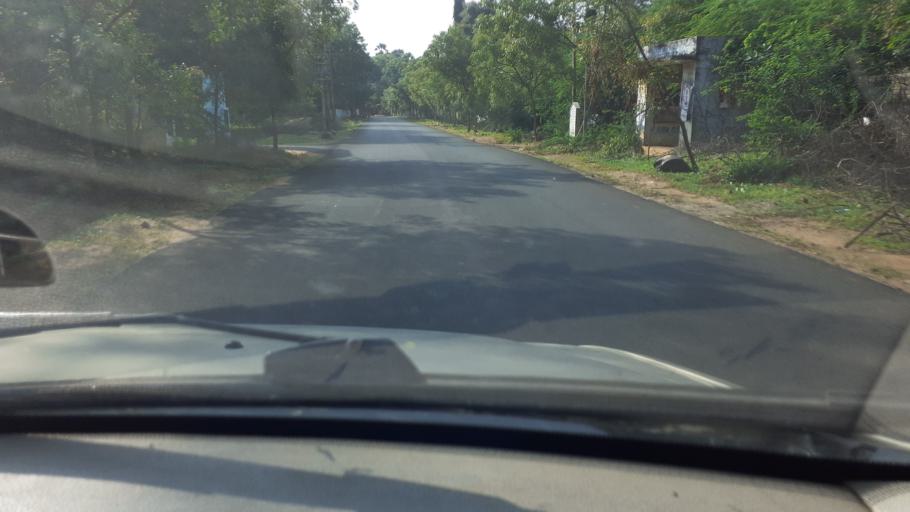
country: IN
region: Tamil Nadu
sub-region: Thoothukkudi
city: Eral
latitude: 8.5788
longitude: 78.0251
